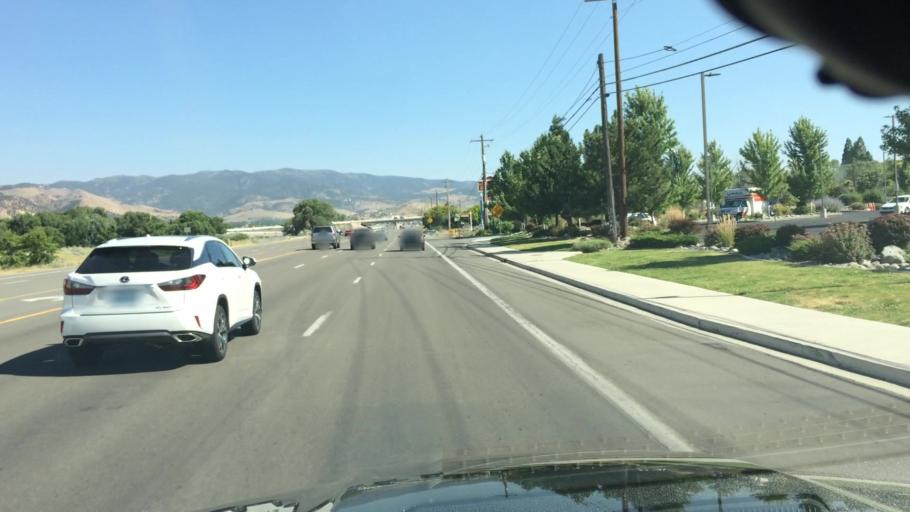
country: US
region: Nevada
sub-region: Washoe County
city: Sparks
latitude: 39.4155
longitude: -119.7546
